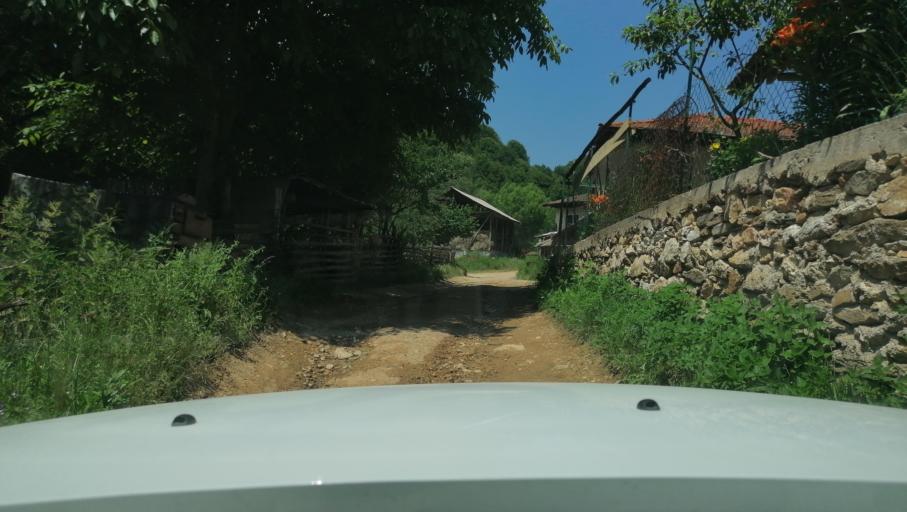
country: MK
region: Berovo
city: Berovo
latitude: 41.5944
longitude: 22.9196
